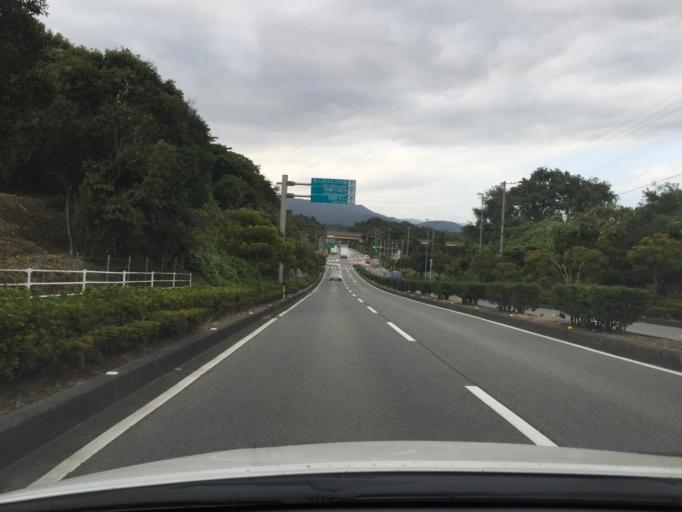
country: JP
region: Ibaraki
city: Kitaibaraki
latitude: 36.9036
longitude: 140.7550
